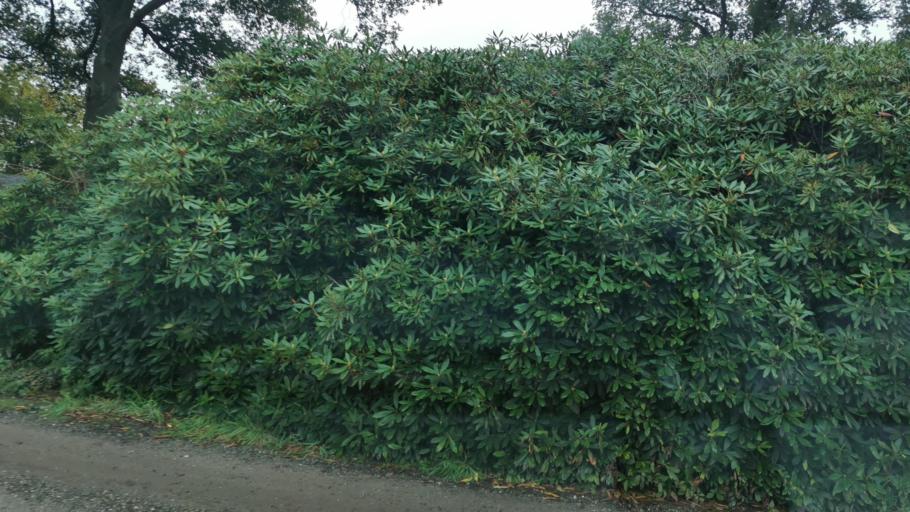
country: NL
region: Overijssel
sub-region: Gemeente Oldenzaal
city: Oldenzaal
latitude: 52.3363
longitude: 6.9708
